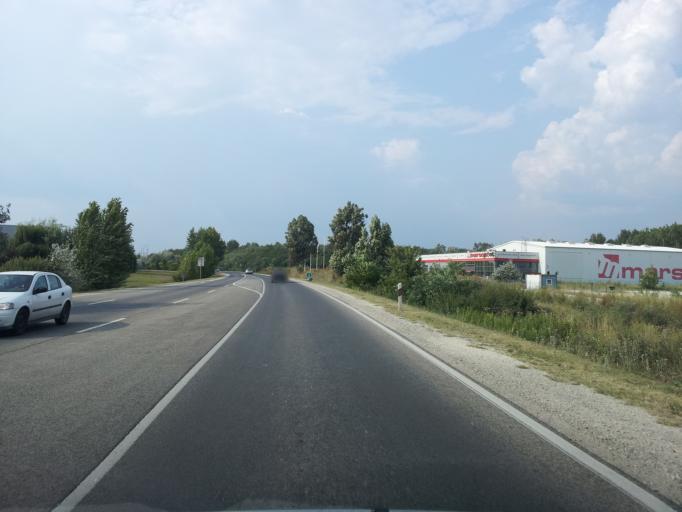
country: HU
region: Pest
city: Dunaharaszti
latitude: 47.3561
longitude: 19.1239
